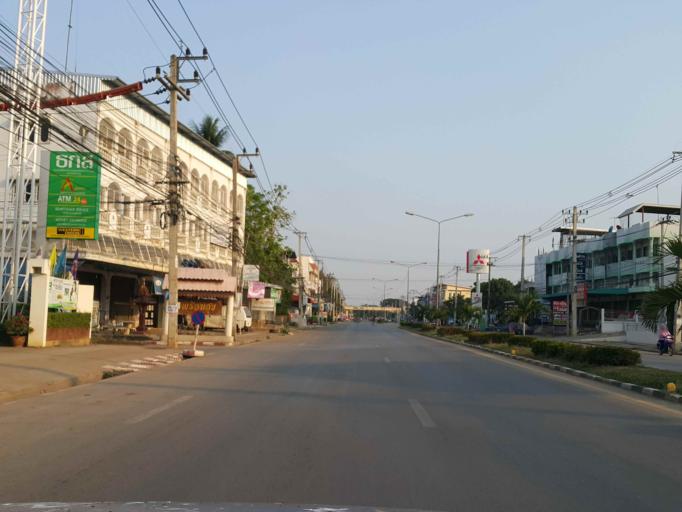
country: TH
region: Sukhothai
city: Sawankhalok
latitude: 17.2983
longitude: 99.8357
